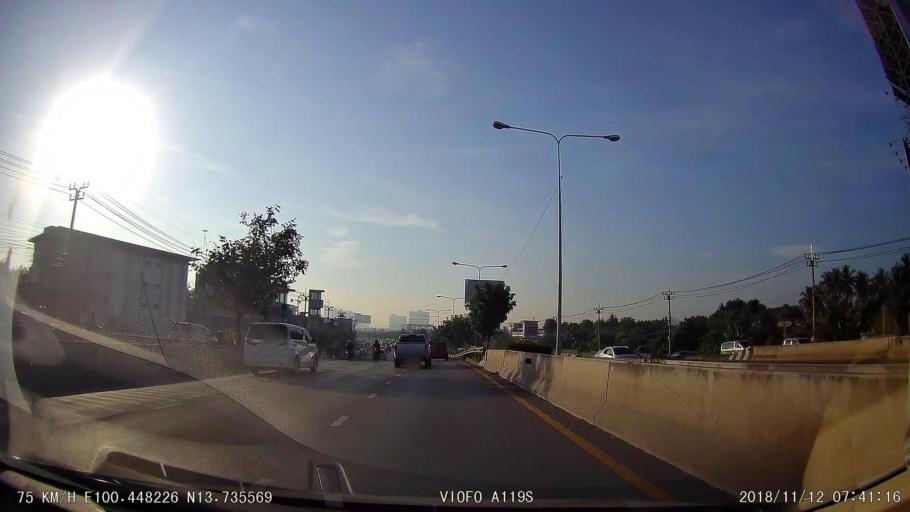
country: TH
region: Bangkok
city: Phasi Charoen
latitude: 13.7346
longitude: 100.4487
